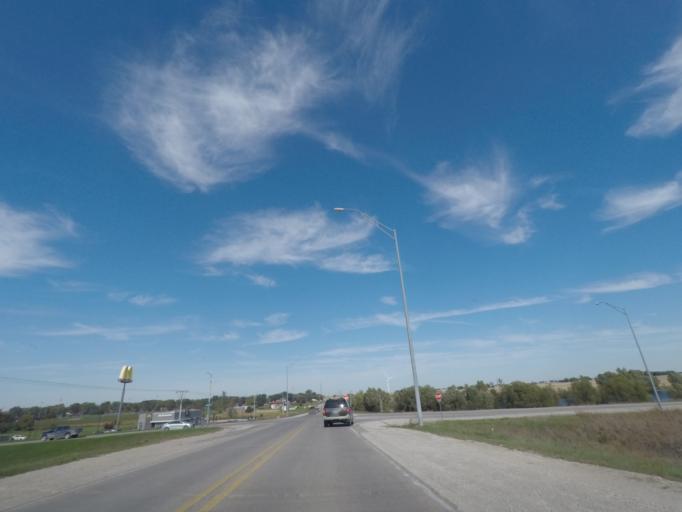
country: US
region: Iowa
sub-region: Story County
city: Nevada
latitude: 42.0092
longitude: -93.4349
